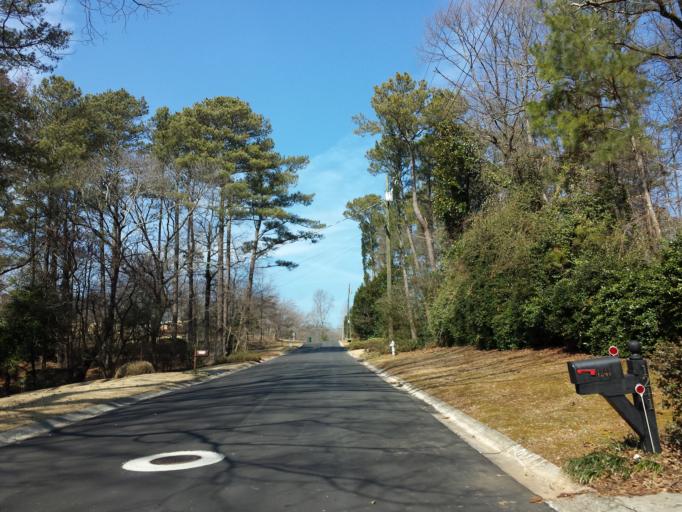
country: US
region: Georgia
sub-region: Cobb County
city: Vinings
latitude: 33.9208
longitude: -84.4581
